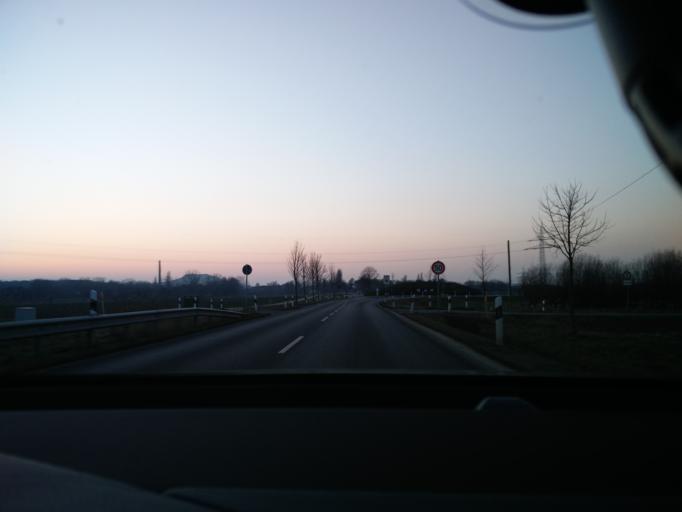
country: DE
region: Lower Saxony
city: Sehnde
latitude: 52.3177
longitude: 9.9918
